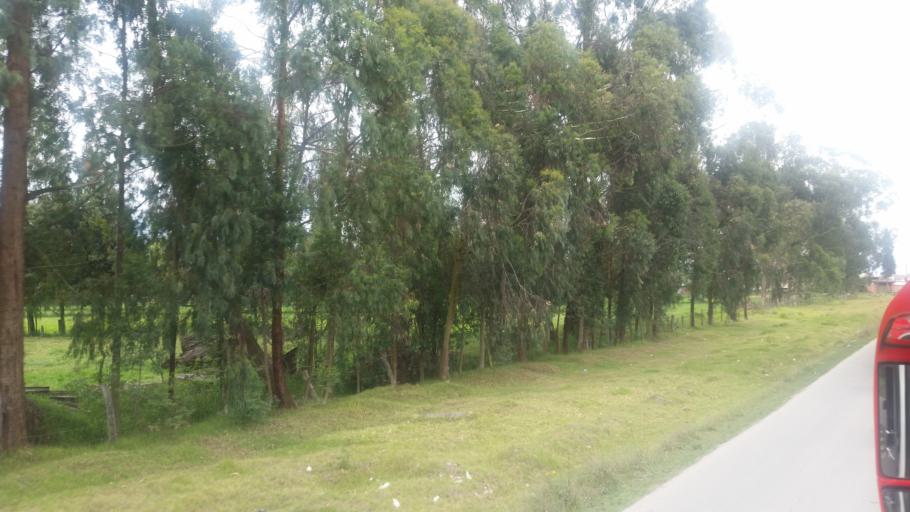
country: CO
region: Cundinamarca
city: Cogua
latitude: 5.0405
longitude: -73.9563
